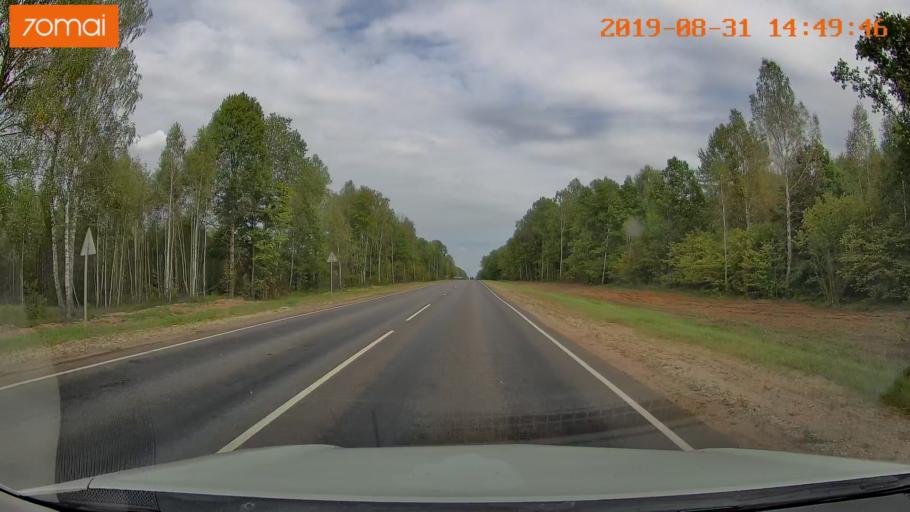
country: RU
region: Kaluga
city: Spas-Demensk
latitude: 54.2565
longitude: 33.7731
